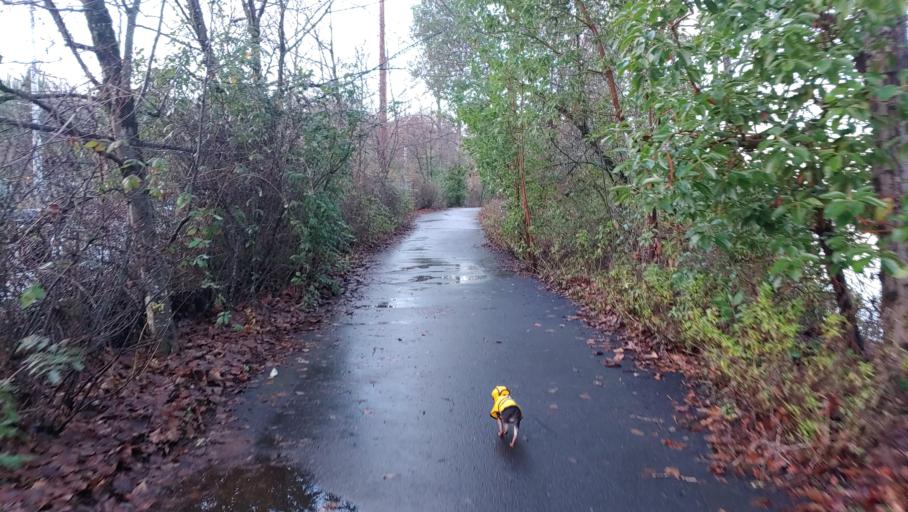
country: US
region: Washington
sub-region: King County
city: White Center
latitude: 47.5571
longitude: -122.3502
